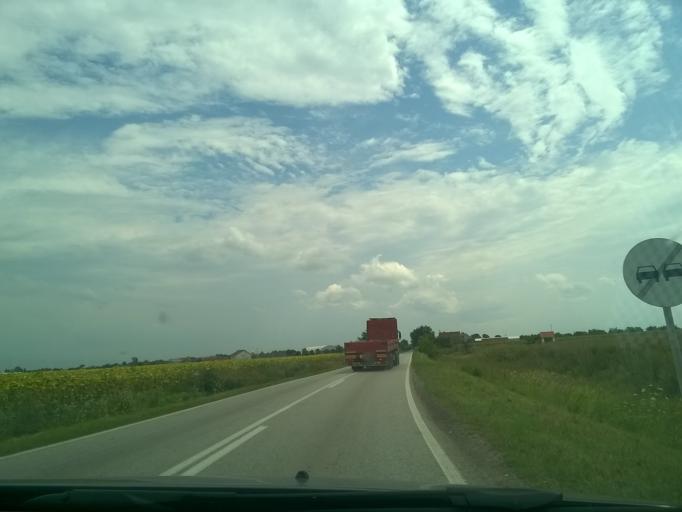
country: RS
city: Lazarevo
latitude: 45.3888
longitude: 20.5207
